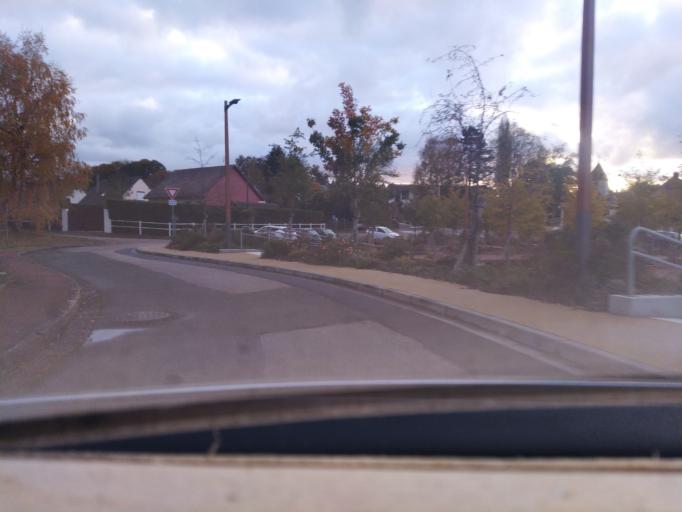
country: FR
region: Haute-Normandie
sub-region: Departement de la Seine-Maritime
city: Yainville
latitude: 49.4553
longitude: 0.8321
